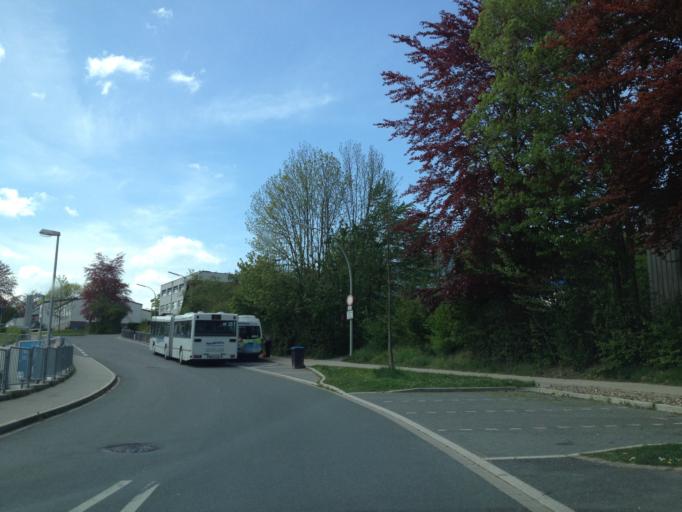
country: DE
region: North Rhine-Westphalia
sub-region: Regierungsbezirk Arnsberg
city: Mohnesee
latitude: 51.4996
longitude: 8.1314
